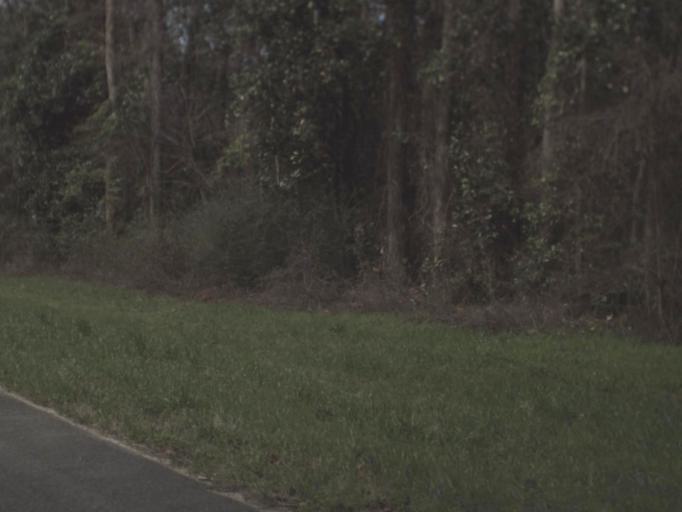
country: US
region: Florida
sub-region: Gadsden County
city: Gretna
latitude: 30.5348
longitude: -84.7694
